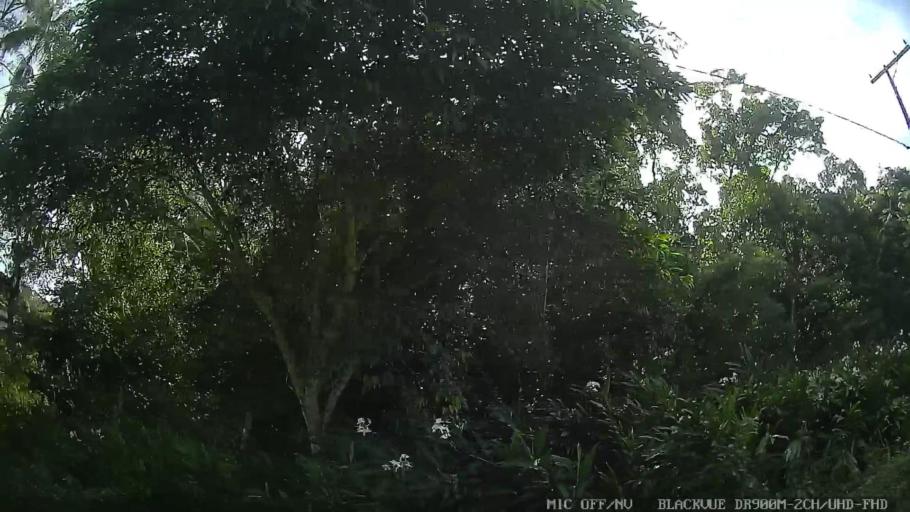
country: BR
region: Sao Paulo
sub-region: Peruibe
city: Peruibe
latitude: -24.2251
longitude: -46.9183
